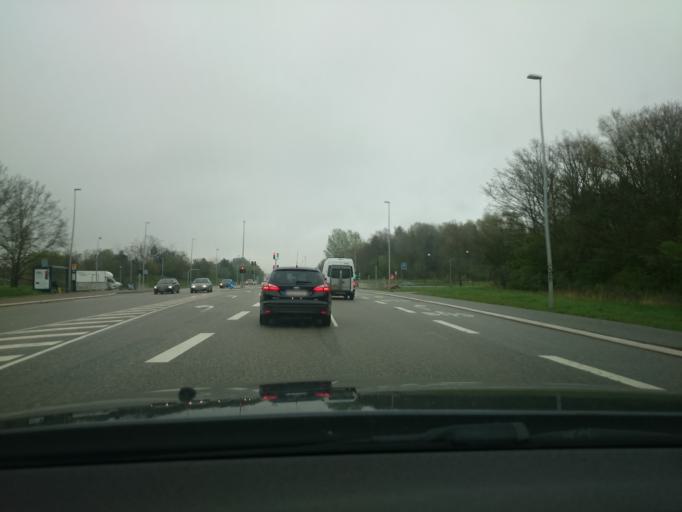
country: DK
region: Capital Region
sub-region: Ballerup Kommune
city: Ballerup
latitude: 55.7484
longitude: 12.3981
